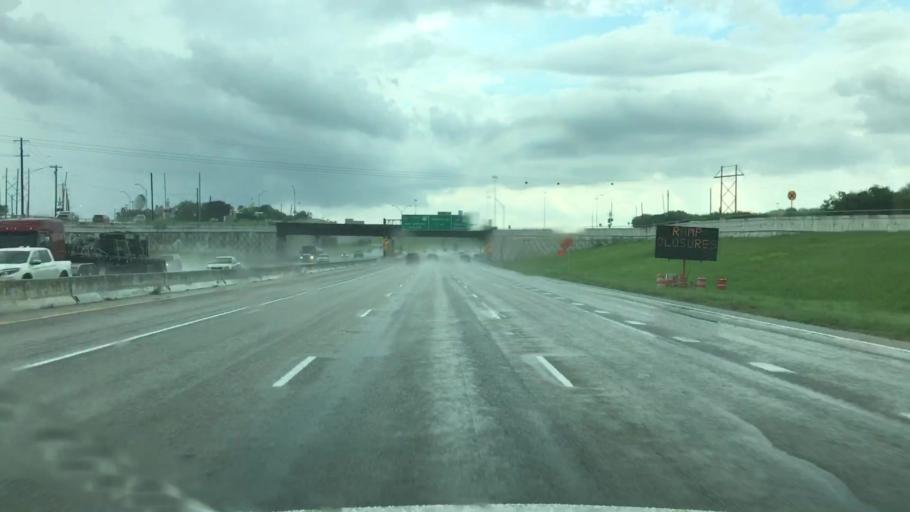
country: US
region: Texas
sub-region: Nueces County
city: Robstown
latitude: 27.8613
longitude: -97.6147
